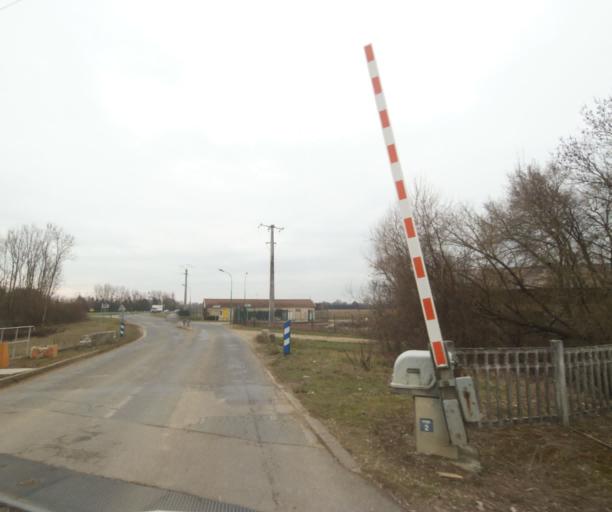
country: FR
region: Champagne-Ardenne
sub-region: Departement de la Haute-Marne
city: Villiers-en-Lieu
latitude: 48.6576
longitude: 4.9092
